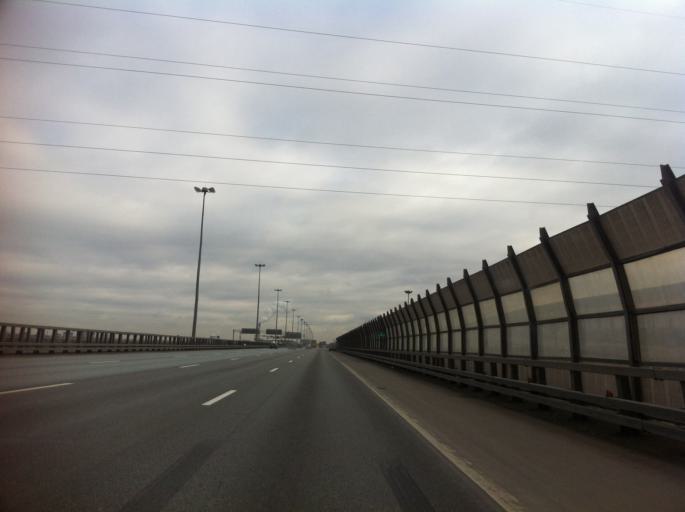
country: RU
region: St.-Petersburg
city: Shushary
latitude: 59.8151
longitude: 30.3761
